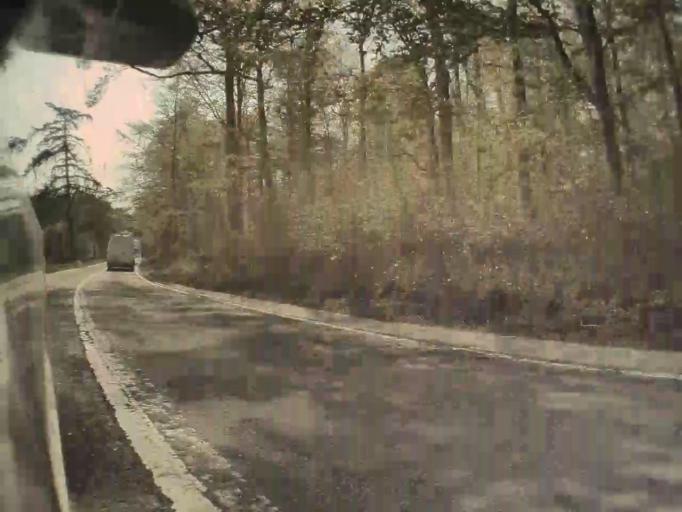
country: BE
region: Wallonia
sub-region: Province de Namur
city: Hamois
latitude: 50.2930
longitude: 5.2053
